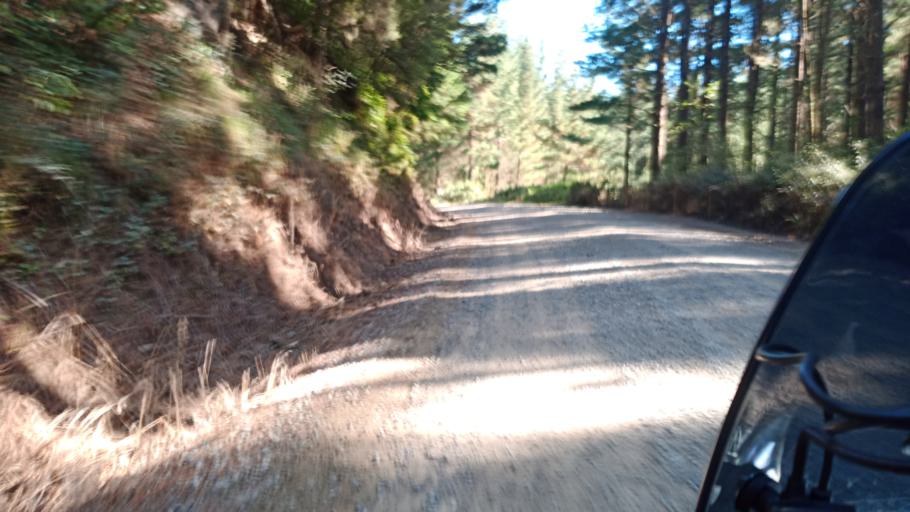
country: NZ
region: Hawke's Bay
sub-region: Wairoa District
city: Wairoa
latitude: -38.9297
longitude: 177.2239
